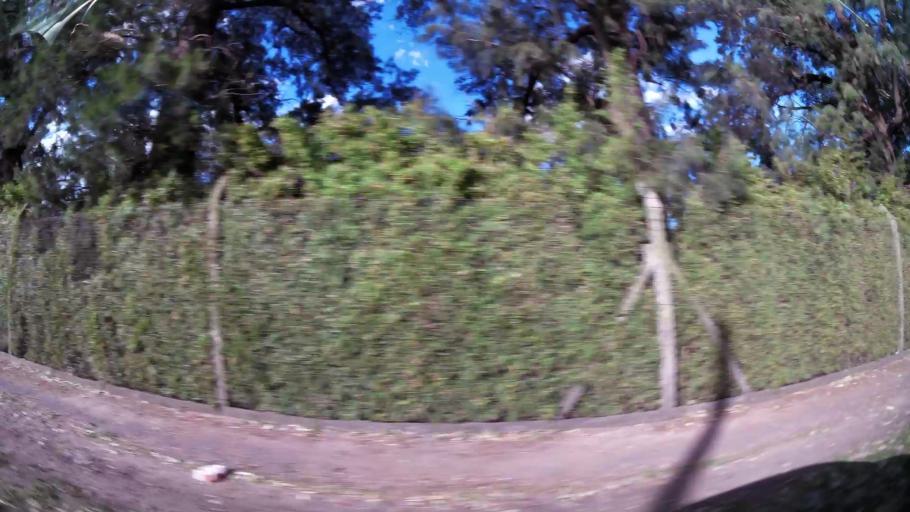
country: AR
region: Buenos Aires
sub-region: Partido de San Isidro
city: San Isidro
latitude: -34.4909
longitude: -58.5559
